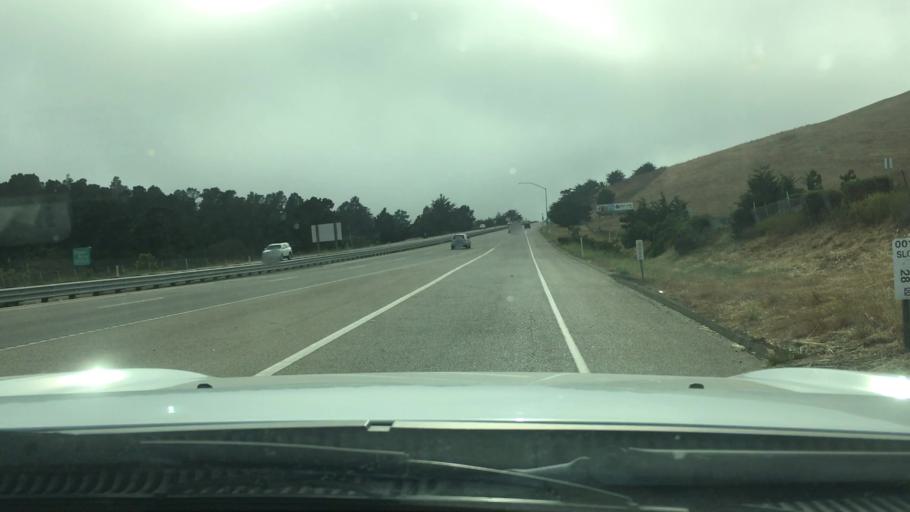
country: US
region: California
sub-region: San Luis Obispo County
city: Morro Bay
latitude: 35.3647
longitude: -120.8251
